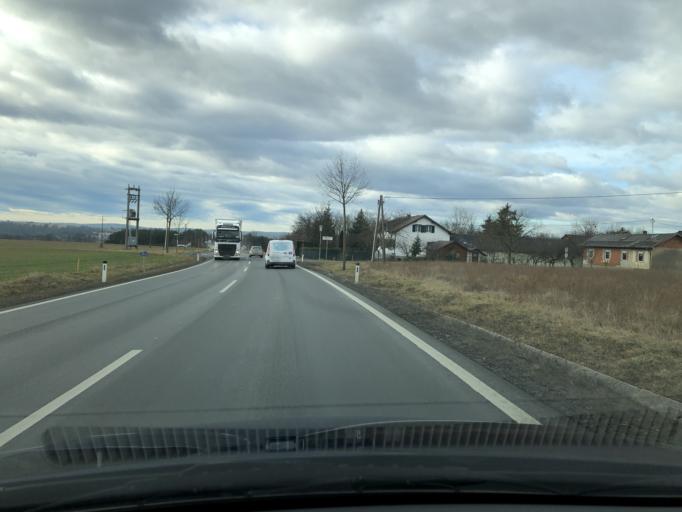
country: AT
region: Burgenland
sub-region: Politischer Bezirk Oberwart
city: Grosspetersdorf
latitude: 47.2571
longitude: 16.3511
